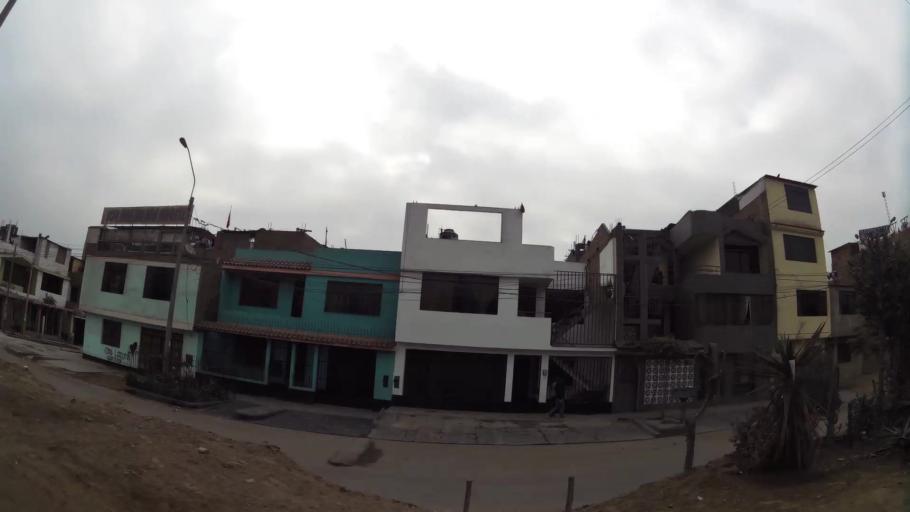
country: PE
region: Lima
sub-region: Lima
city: Independencia
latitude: -11.9774
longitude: -76.9960
